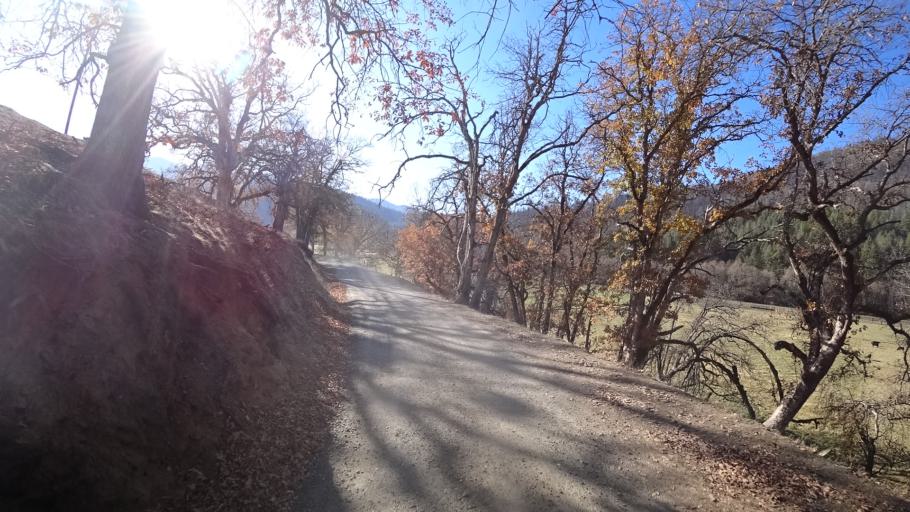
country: US
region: California
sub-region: Siskiyou County
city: Happy Camp
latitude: 41.8338
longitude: -123.0059
